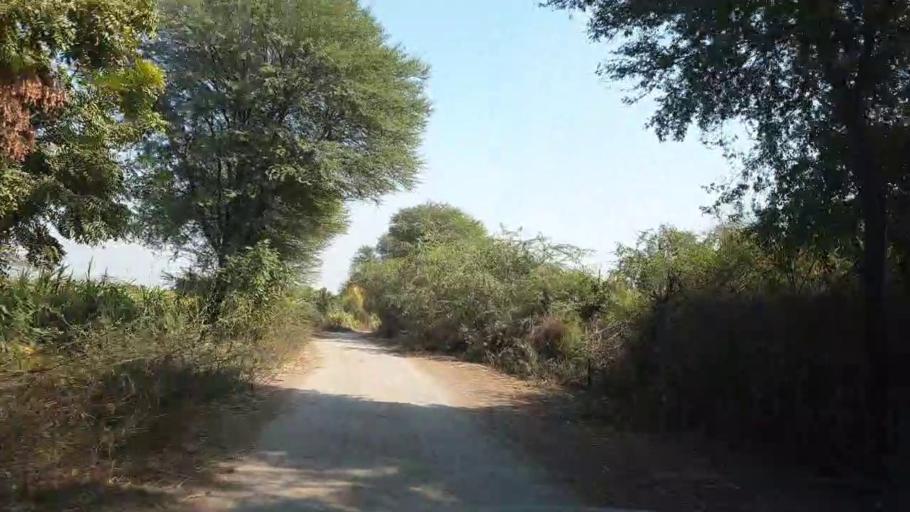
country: PK
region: Sindh
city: Tando Allahyar
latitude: 25.5733
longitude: 68.7323
